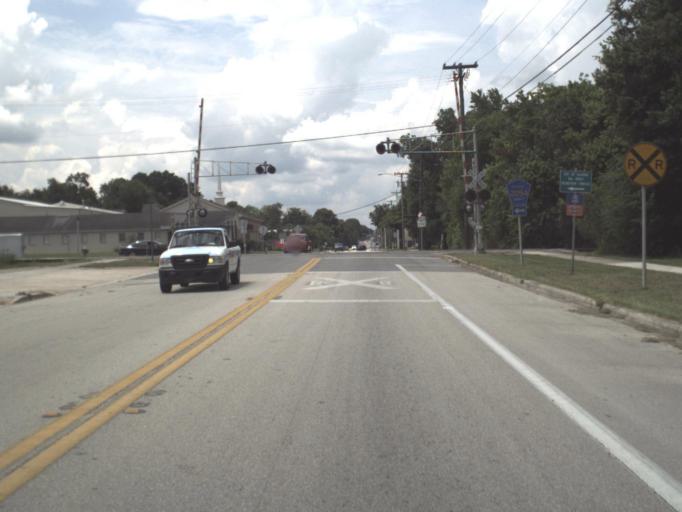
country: US
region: Florida
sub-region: Alachua County
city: Alachua
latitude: 29.7869
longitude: -82.4942
